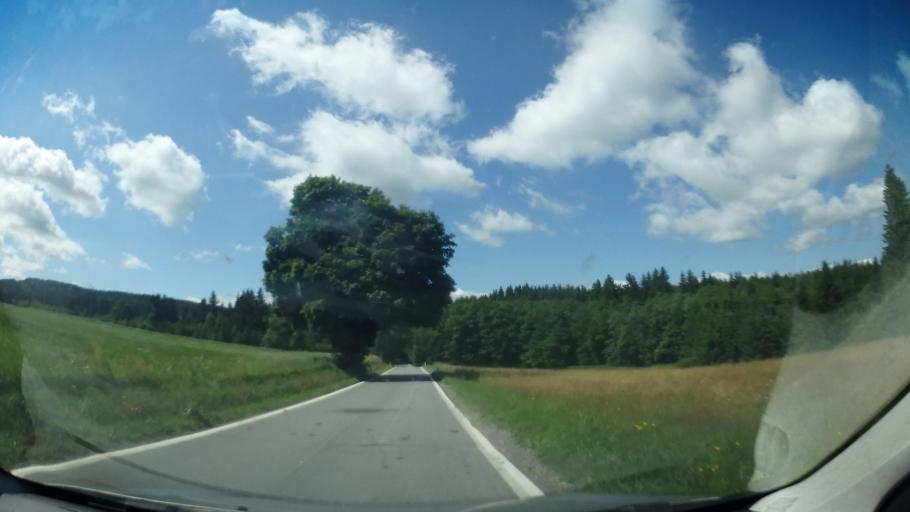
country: CZ
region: Vysocina
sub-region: Okres Zd'ar nad Sazavou
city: Nove Mesto na Morave
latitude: 49.6307
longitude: 16.0758
